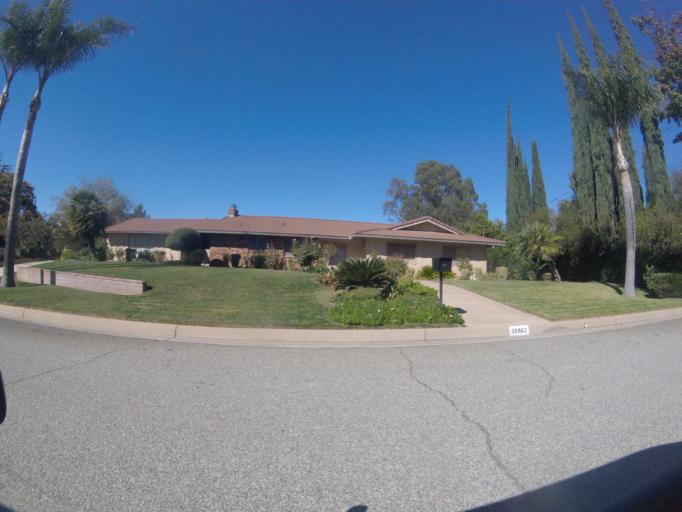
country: US
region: California
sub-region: San Bernardino County
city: Mentone
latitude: 34.0184
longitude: -117.1308
